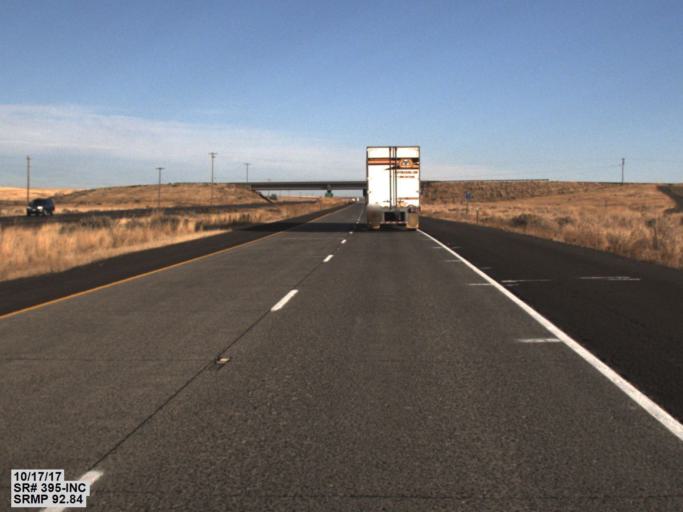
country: US
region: Washington
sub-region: Adams County
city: Ritzville
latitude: 47.0715
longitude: -118.4096
